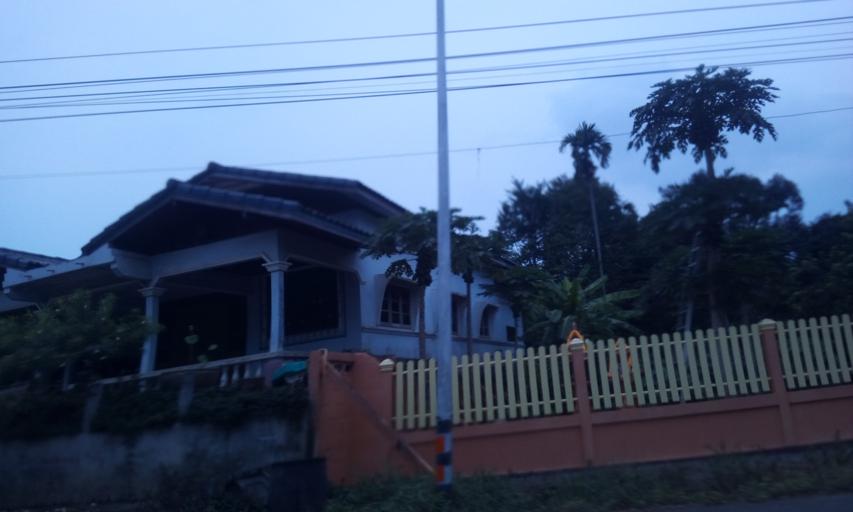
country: TH
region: Trat
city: Laem Ngop
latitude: 12.2566
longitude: 102.2868
